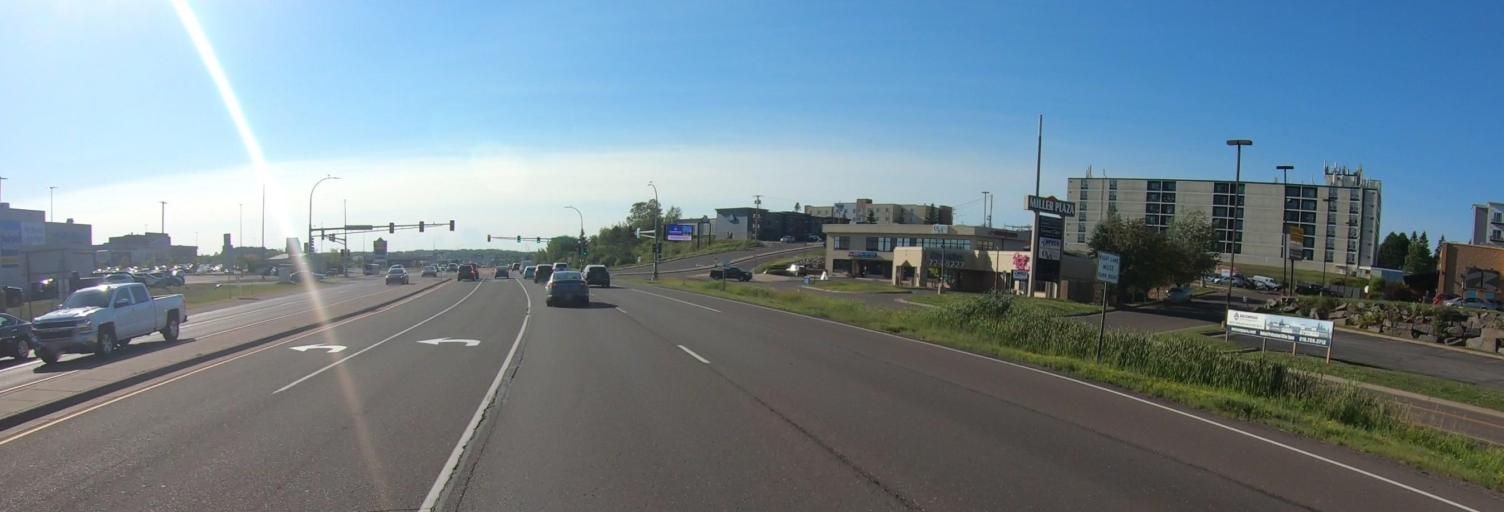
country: US
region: Minnesota
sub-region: Saint Louis County
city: Duluth
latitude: 46.8052
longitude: -92.1556
